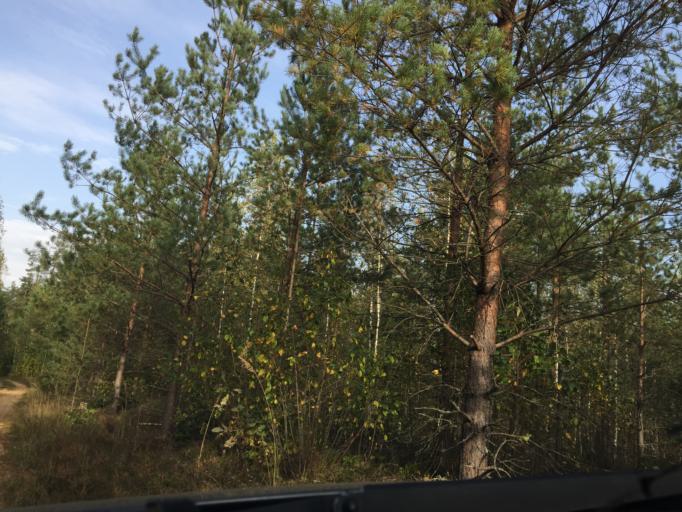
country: LV
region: Garkalne
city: Garkalne
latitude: 56.9718
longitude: 24.4312
